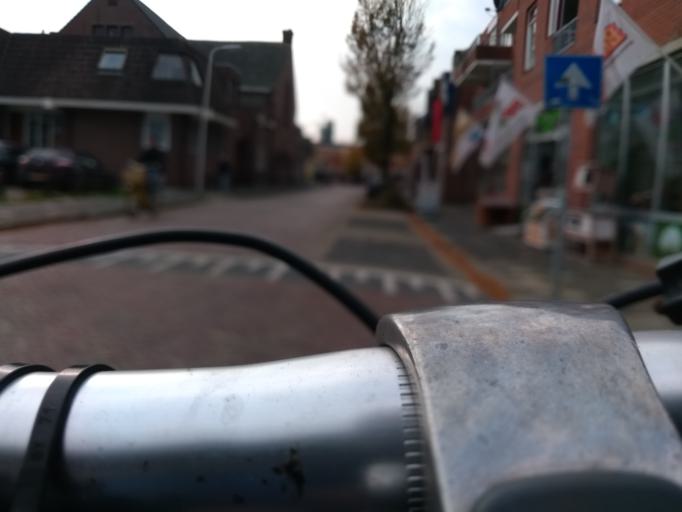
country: NL
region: Drenthe
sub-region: Gemeente Assen
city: Assen
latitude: 52.9970
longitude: 6.5619
